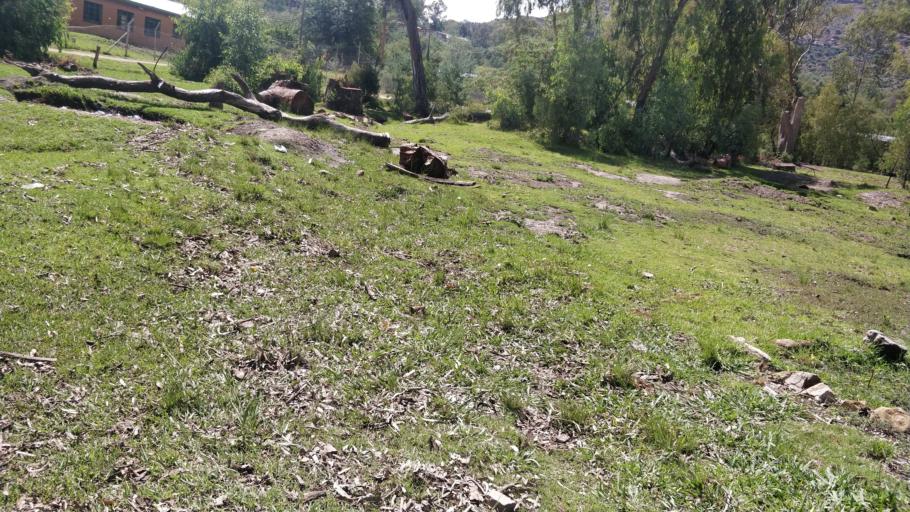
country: LS
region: Maseru
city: Nako
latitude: -29.6288
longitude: 27.5065
